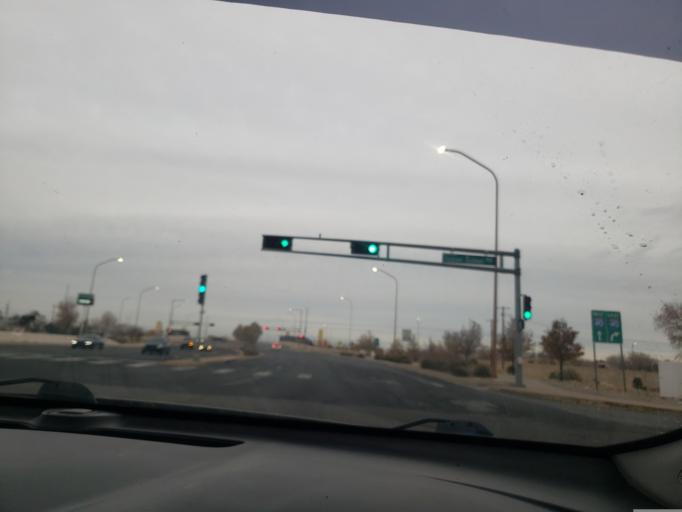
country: US
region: New Mexico
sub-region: Bernalillo County
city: Albuquerque
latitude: 35.1017
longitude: -106.5865
